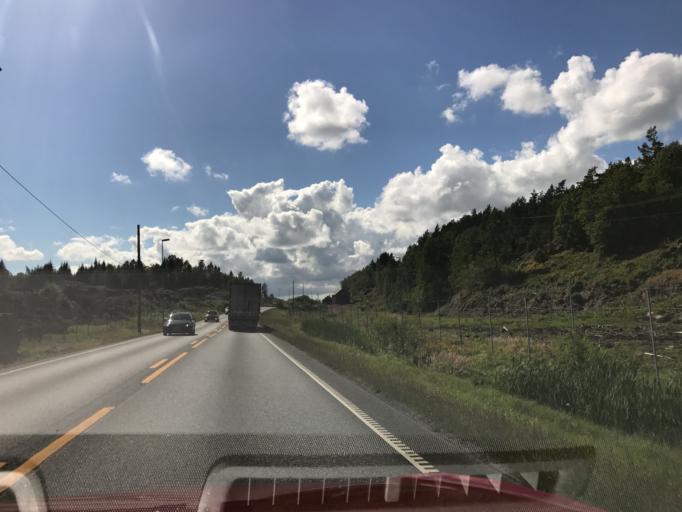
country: NO
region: Telemark
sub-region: Bamble
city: Herre
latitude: 58.9726
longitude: 9.5138
